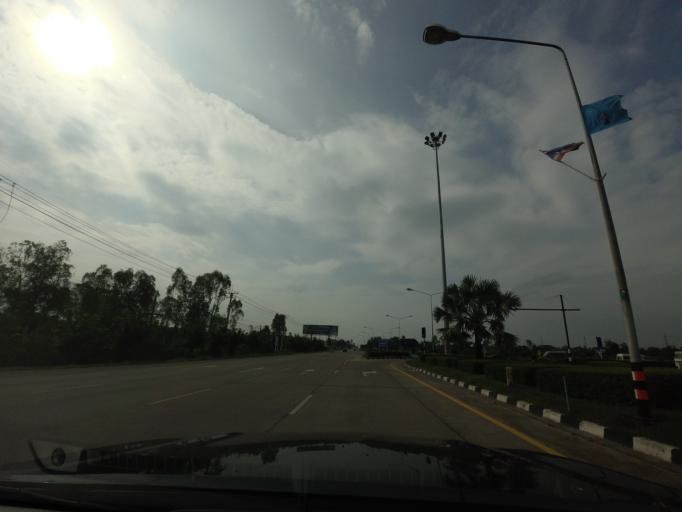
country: TH
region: Nong Khai
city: Nong Khai
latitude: 17.8133
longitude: 102.7590
